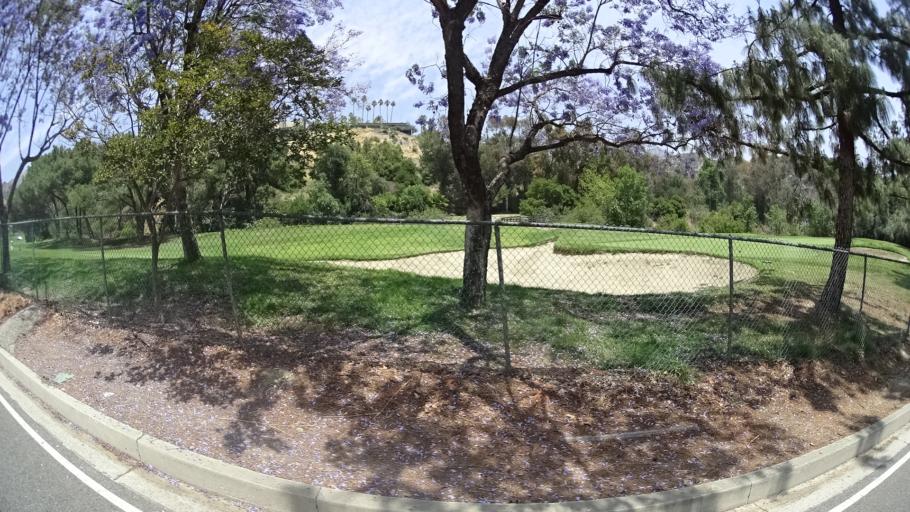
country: US
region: California
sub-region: Los Angeles County
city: Burbank
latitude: 34.2026
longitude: -118.3048
